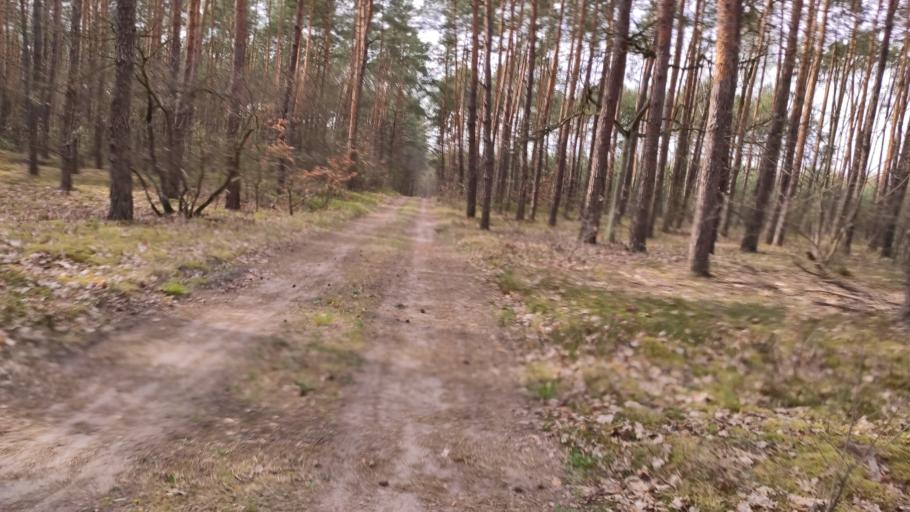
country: PL
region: Masovian Voivodeship
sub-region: Powiat grojecki
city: Warka
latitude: 51.7657
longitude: 21.1957
